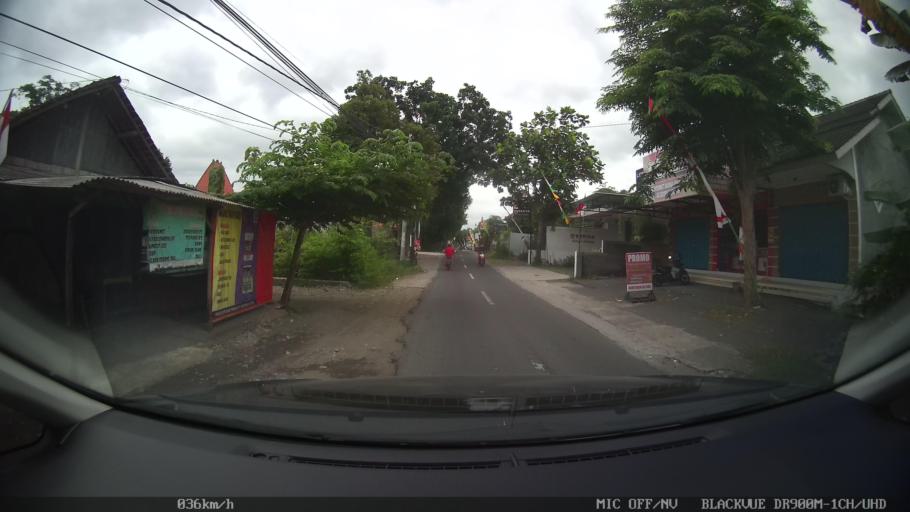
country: ID
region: Daerah Istimewa Yogyakarta
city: Depok
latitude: -7.8142
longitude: 110.4173
